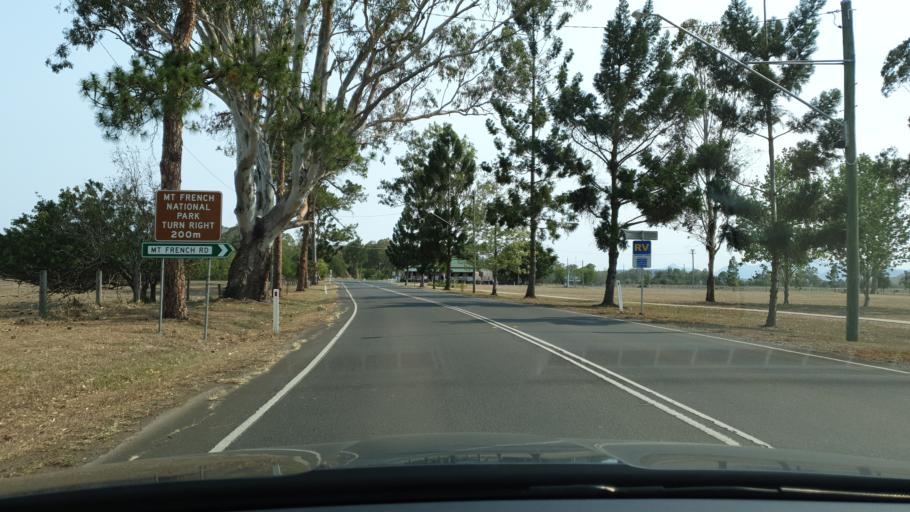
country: AU
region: Queensland
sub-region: Ipswich
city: Deebing Heights
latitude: -28.0025
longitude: 152.6814
